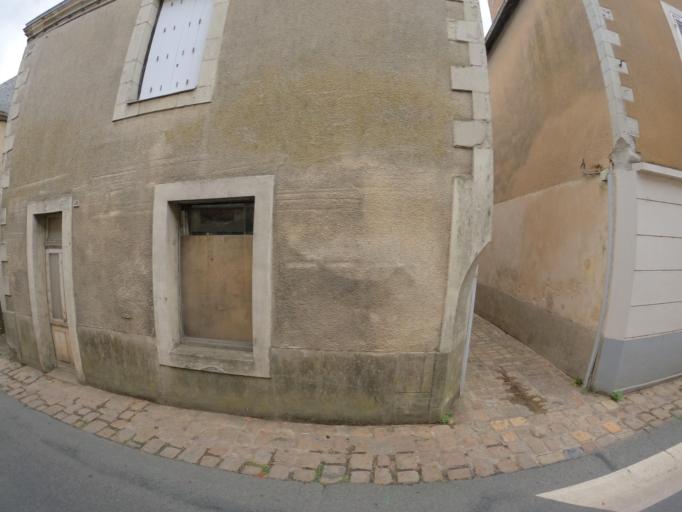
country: FR
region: Pays de la Loire
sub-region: Departement de Maine-et-Loire
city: Morannes
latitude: 47.7914
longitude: -0.4414
